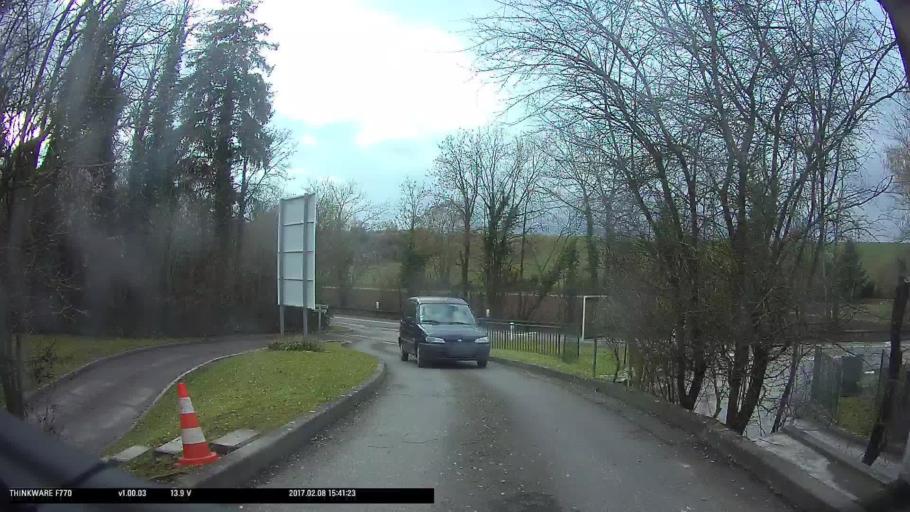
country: FR
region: Ile-de-France
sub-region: Departement du Val-d'Oise
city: Vigny
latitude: 49.0698
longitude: 1.9219
